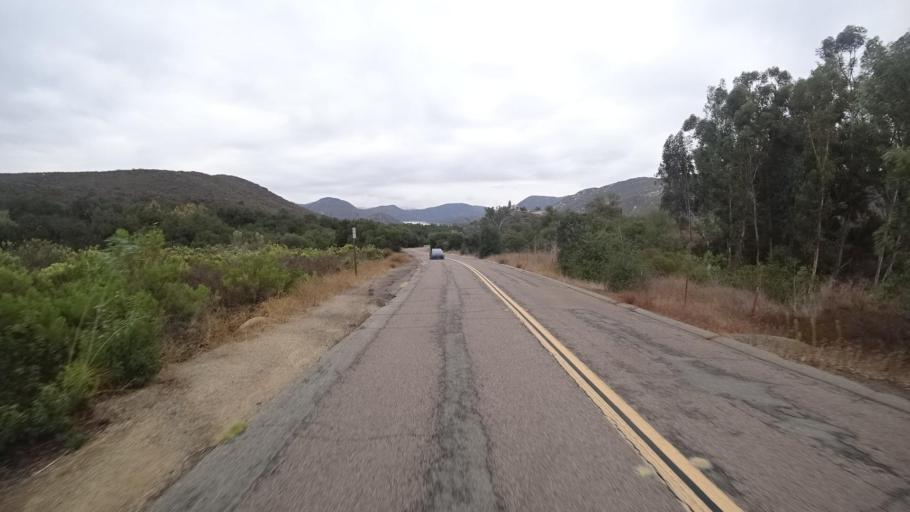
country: US
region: California
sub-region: San Diego County
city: Escondido
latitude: 33.0862
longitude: -117.1144
